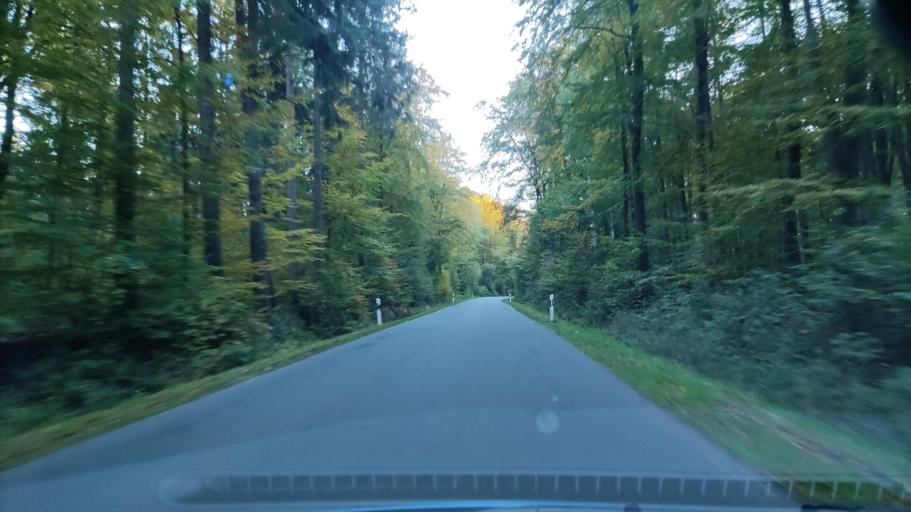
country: DE
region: Schleswig-Holstein
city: Schwarzenbek
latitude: 53.5201
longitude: 10.4587
